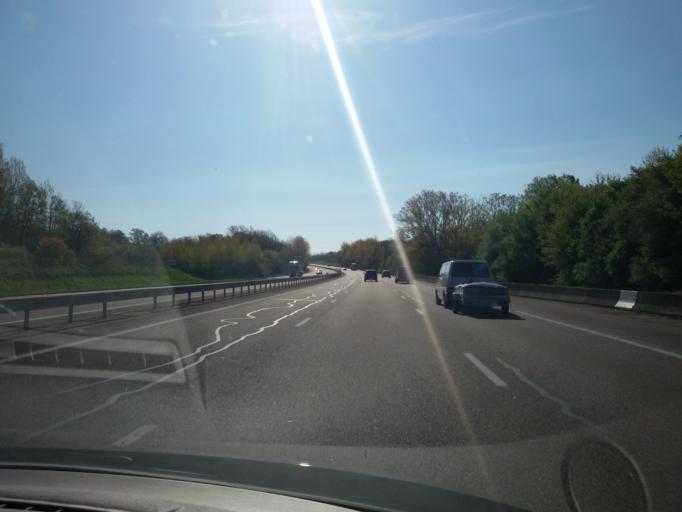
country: FR
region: Bourgogne
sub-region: Departement de l'Yonne
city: Fleury-la-Vallee
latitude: 47.8810
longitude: 3.4378
